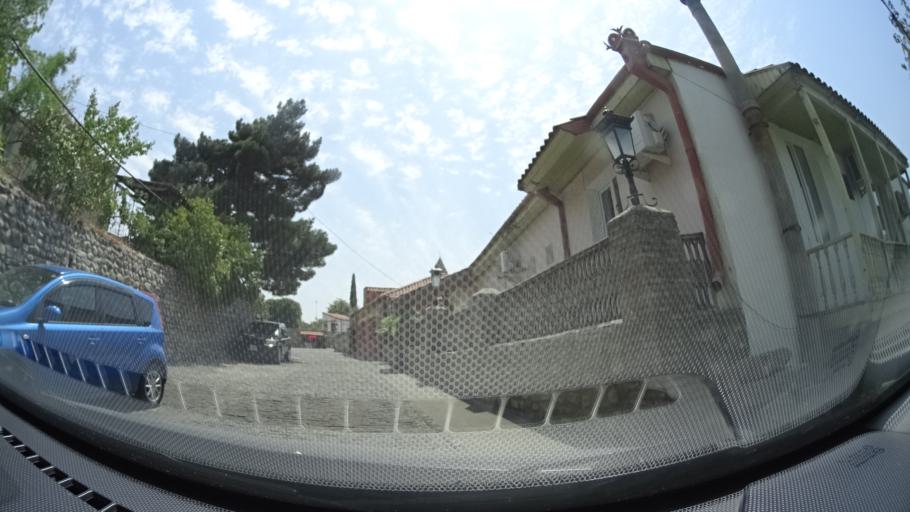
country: GE
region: Kakheti
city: Sighnaghi
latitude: 41.6235
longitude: 45.9236
